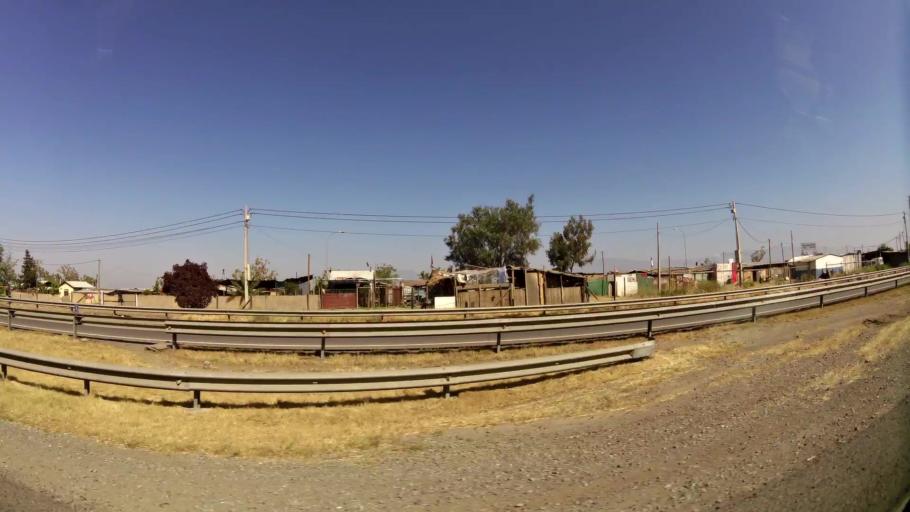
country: CL
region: Santiago Metropolitan
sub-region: Provincia de Chacabuco
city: Chicureo Abajo
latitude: -33.3230
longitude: -70.7058
